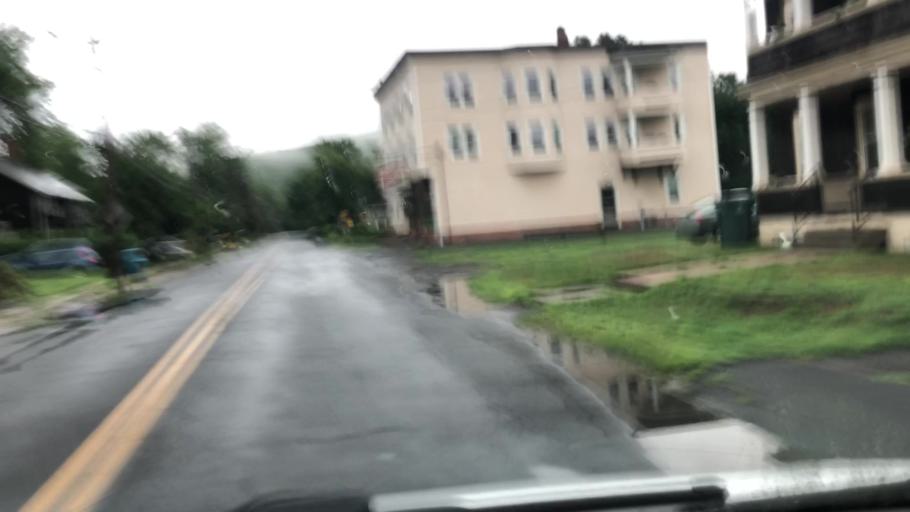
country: US
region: Massachusetts
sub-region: Hampshire County
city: Easthampton
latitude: 42.2757
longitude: -72.6523
